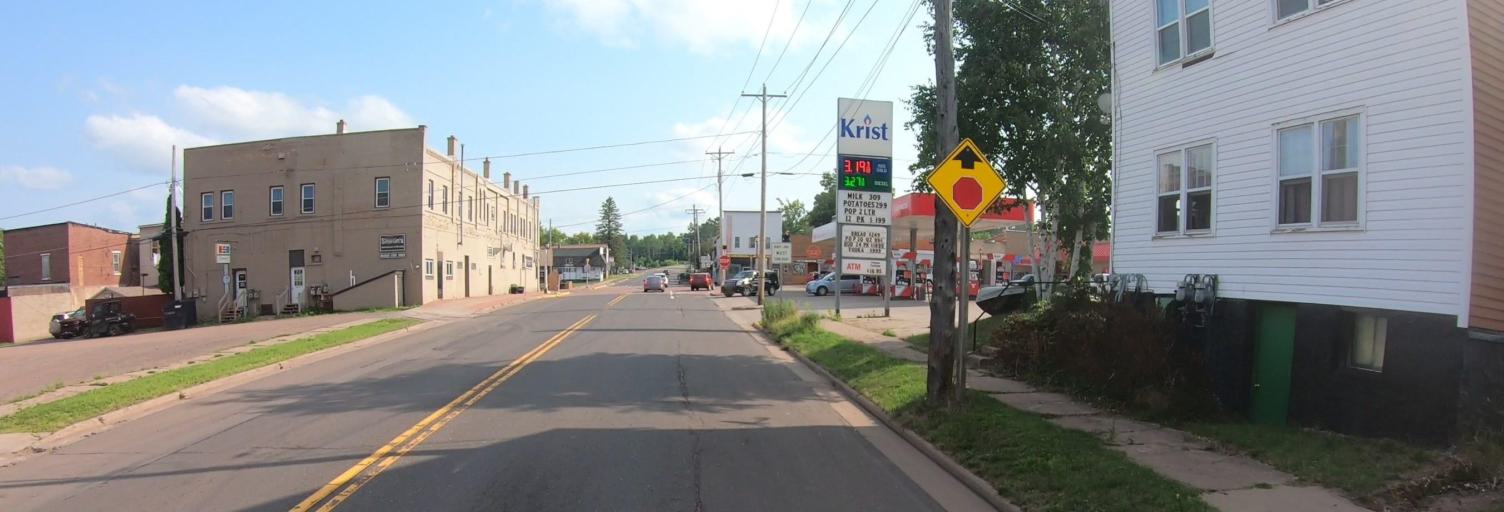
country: US
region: Wisconsin
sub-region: Iron County
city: Hurley
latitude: 46.4507
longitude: -90.1819
